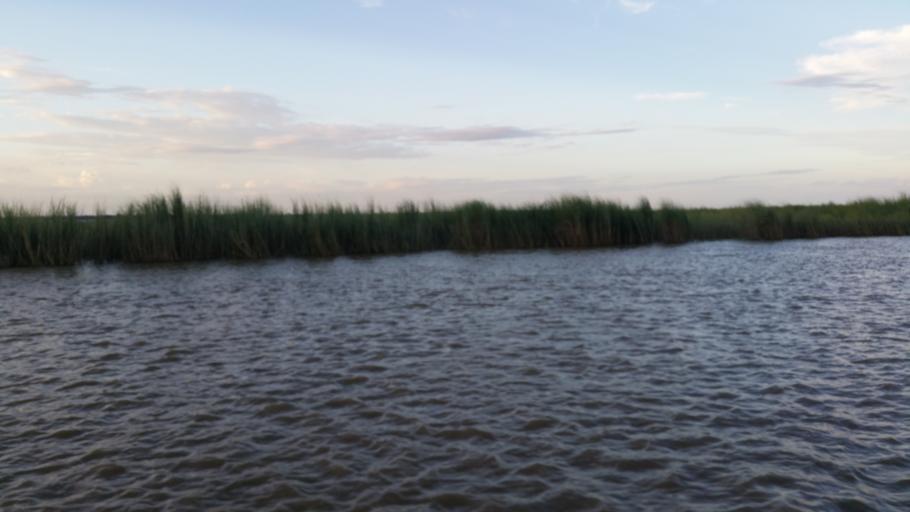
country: MM
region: Magway
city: Pakokku
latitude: 21.1950
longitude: 94.8761
